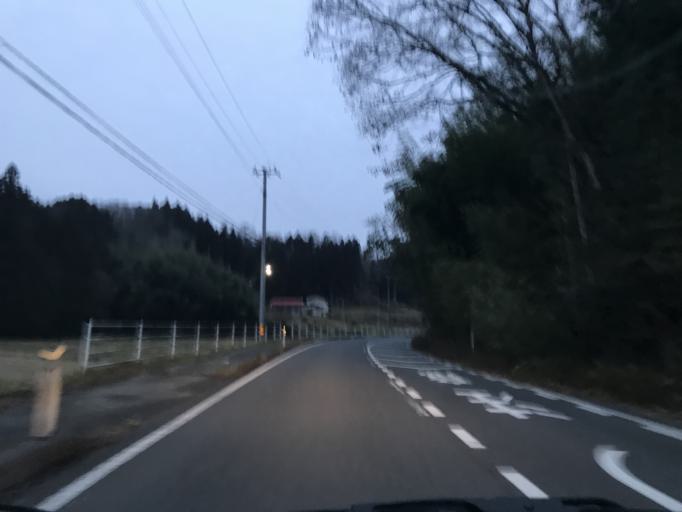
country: JP
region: Iwate
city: Ichinoseki
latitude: 38.8114
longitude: 141.1166
